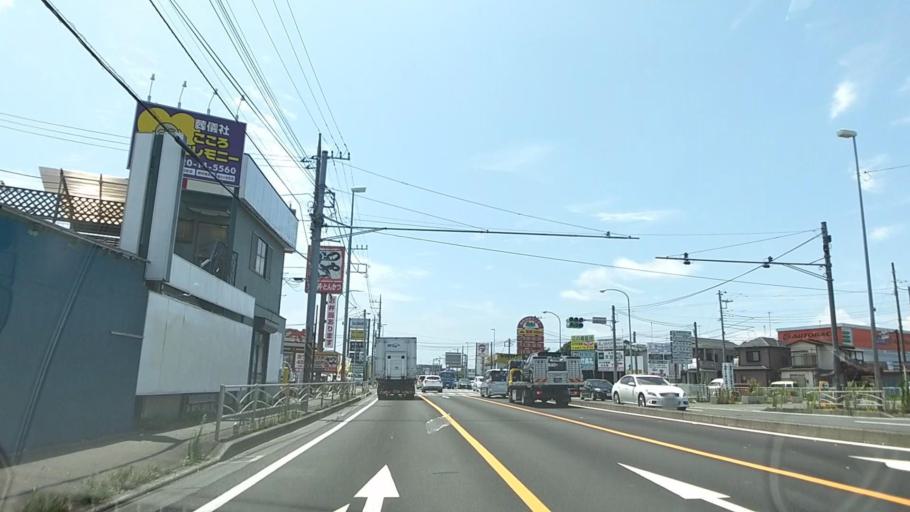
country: JP
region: Kanagawa
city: Zama
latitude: 35.4767
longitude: 139.4159
